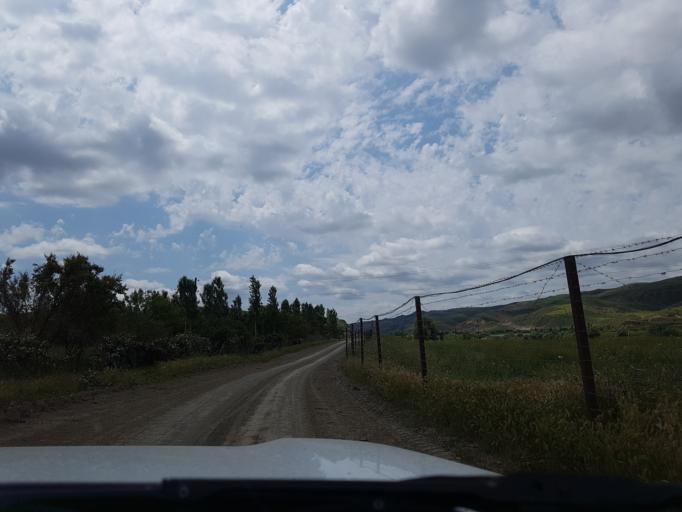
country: TM
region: Ahal
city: Baharly
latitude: 38.2149
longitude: 56.9946
